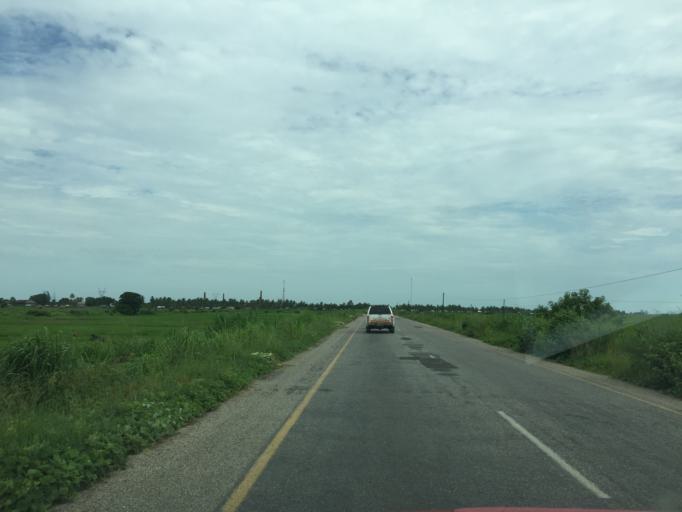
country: MZ
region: Zambezia
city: Quelimane
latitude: -17.7243
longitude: 36.9000
